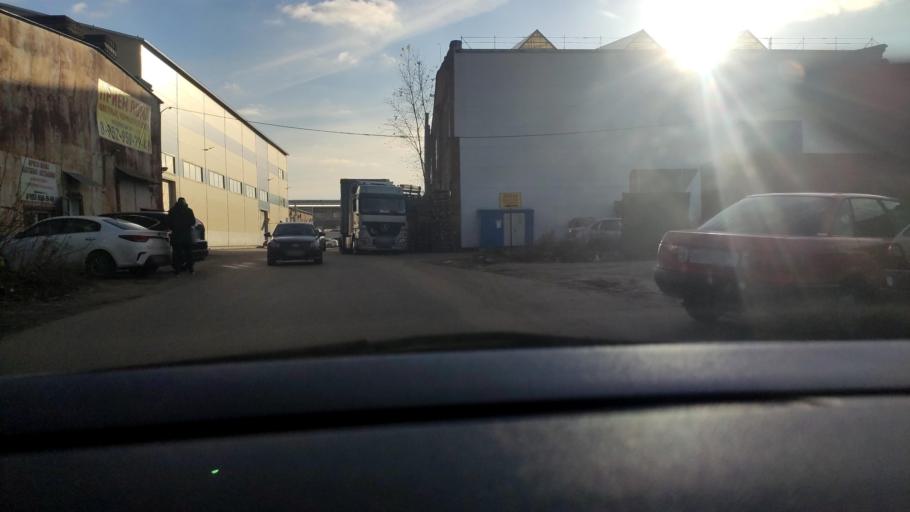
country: RU
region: Voronezj
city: Voronezh
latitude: 51.6905
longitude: 39.1754
